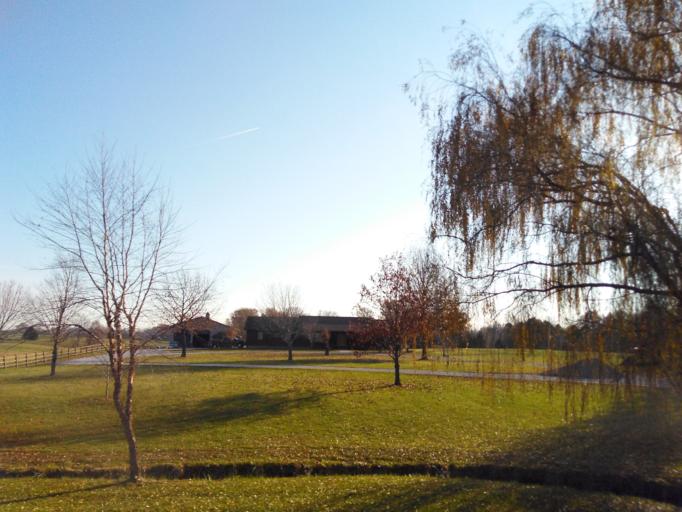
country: US
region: Illinois
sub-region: Madison County
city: Saint Jacob
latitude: 38.7378
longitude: -89.8010
